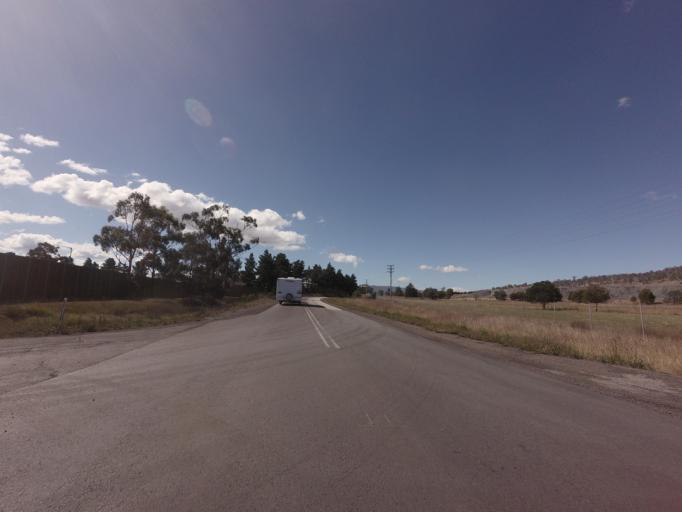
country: AU
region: Tasmania
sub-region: Break O'Day
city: St Helens
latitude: -41.6312
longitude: 147.9856
